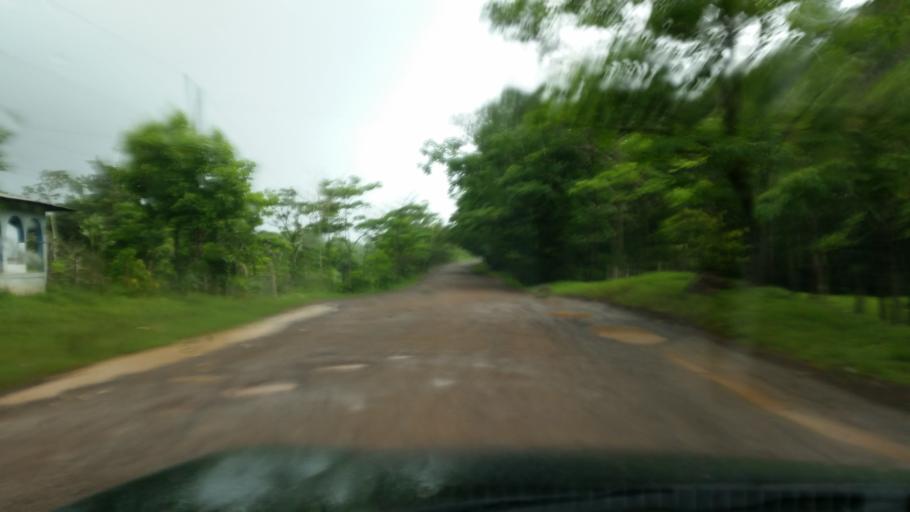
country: NI
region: Atlantico Norte (RAAN)
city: Siuna
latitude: 13.4039
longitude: -84.8539
